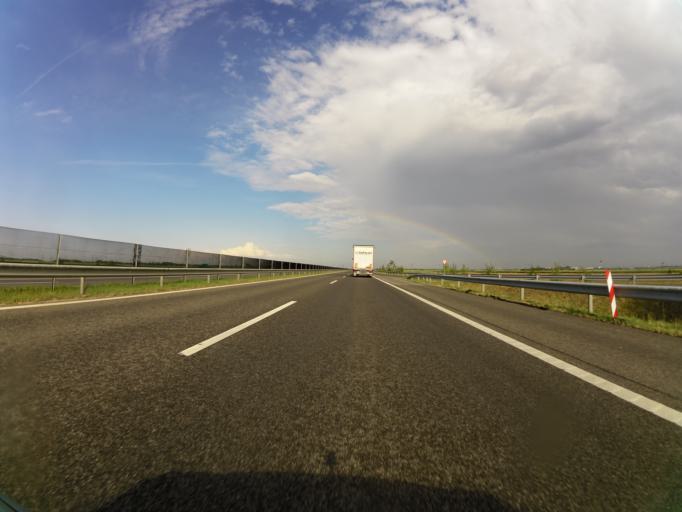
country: HU
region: Csongrad
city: Szeged
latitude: 46.2956
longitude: 20.1116
